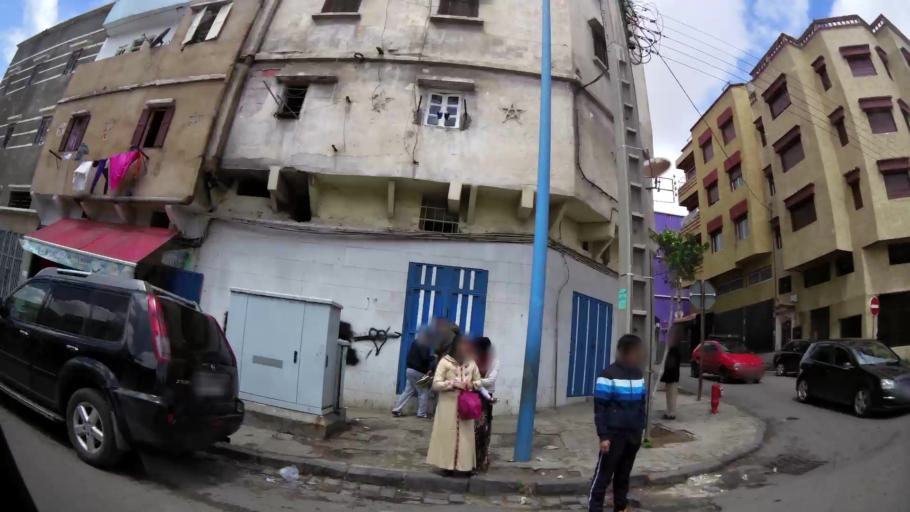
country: MA
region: Grand Casablanca
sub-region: Casablanca
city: Casablanca
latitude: 33.5739
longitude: -7.5925
